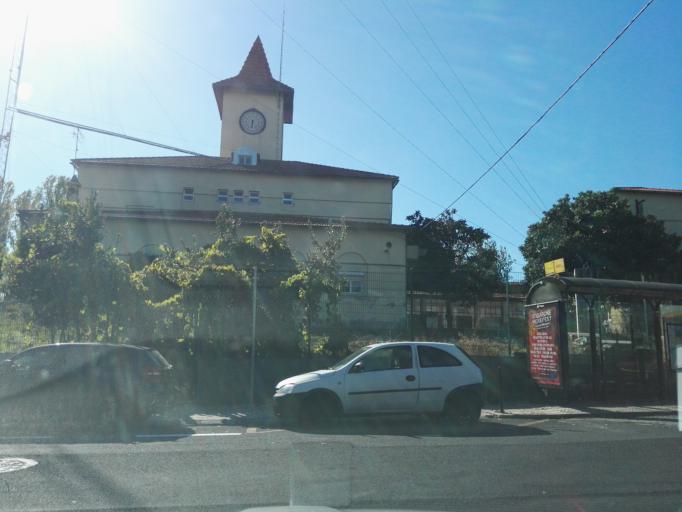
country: PT
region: Lisbon
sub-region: Loures
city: Moscavide
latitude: 38.7703
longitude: -9.1230
